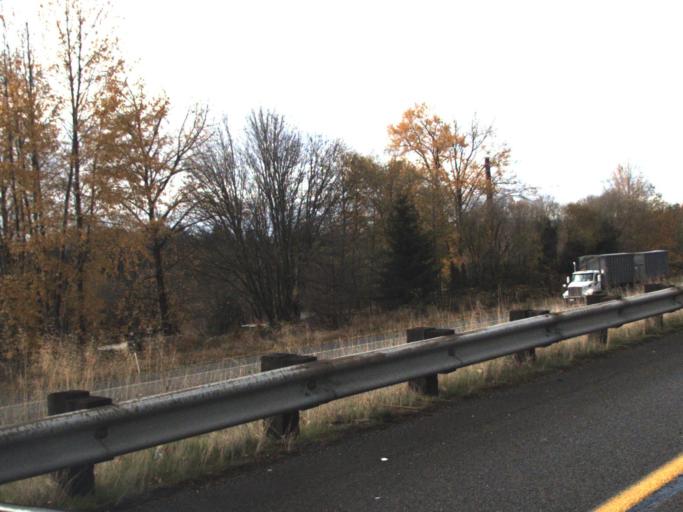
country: US
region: Washington
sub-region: Snohomish County
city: Fobes Hill
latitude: 47.9650
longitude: -122.1275
